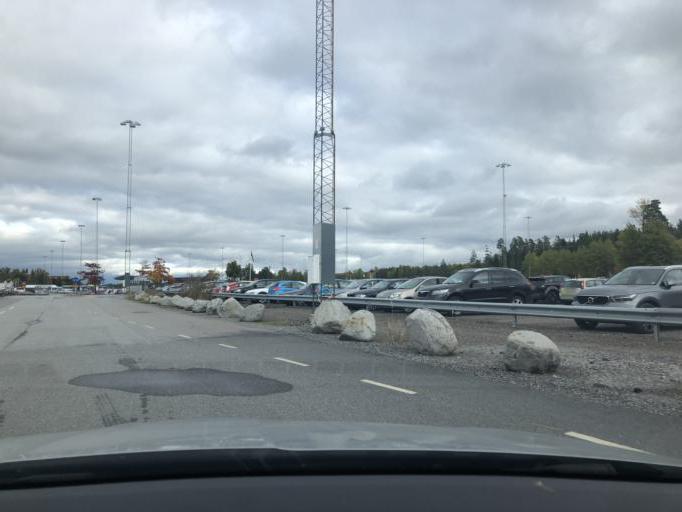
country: SE
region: Stockholm
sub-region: Sigtuna Kommun
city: Rosersberg
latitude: 59.6336
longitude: 17.9349
